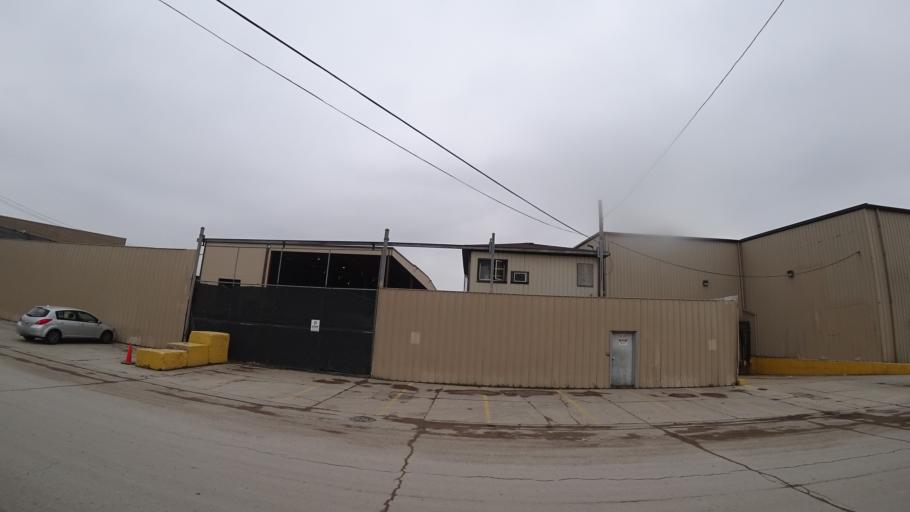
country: US
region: Illinois
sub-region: Cook County
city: Chicago
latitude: 41.8518
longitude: -87.6637
